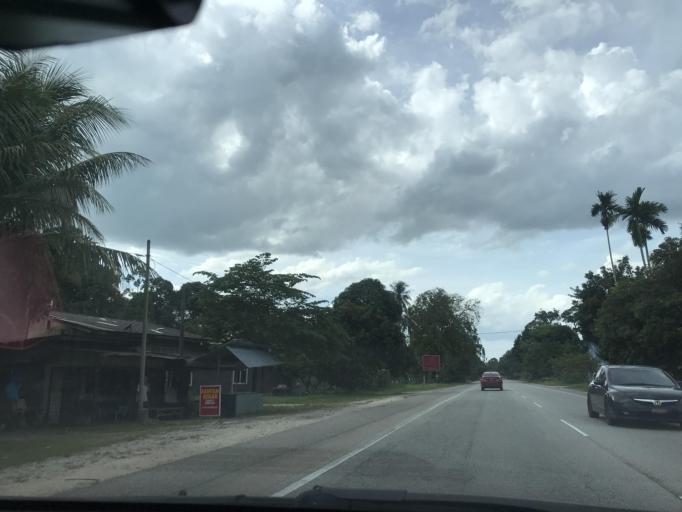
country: MY
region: Kelantan
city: Kampong Pangkal Kalong
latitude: 5.9325
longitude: 102.1912
